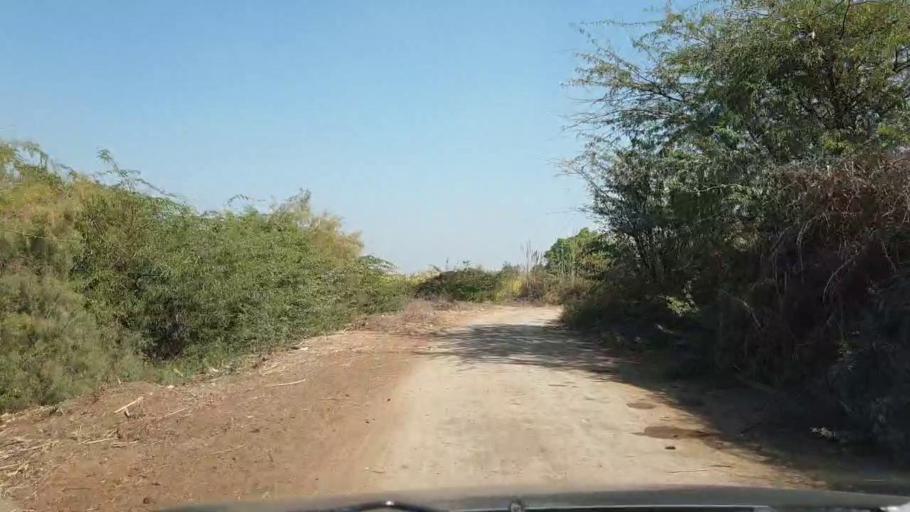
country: PK
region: Sindh
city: Jhol
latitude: 25.9039
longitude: 68.7952
